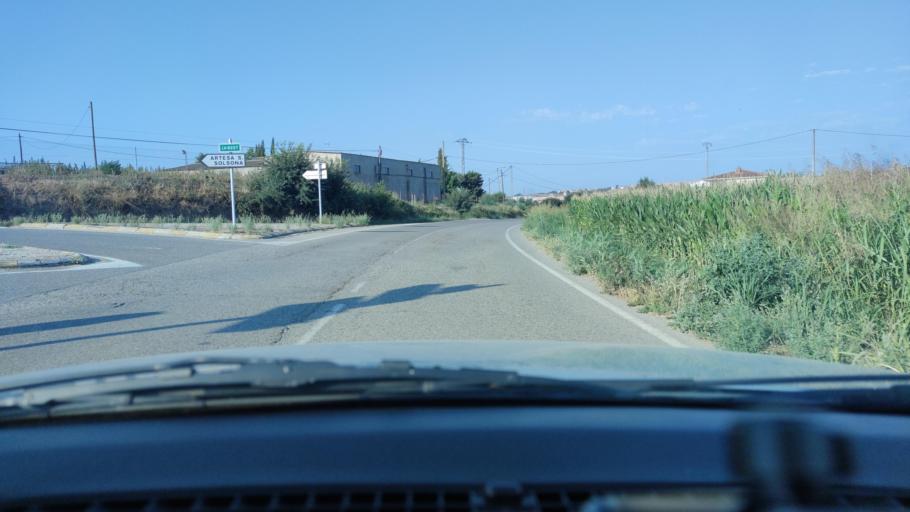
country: ES
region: Catalonia
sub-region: Provincia de Lleida
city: Balaguer
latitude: 41.7983
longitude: 0.8226
